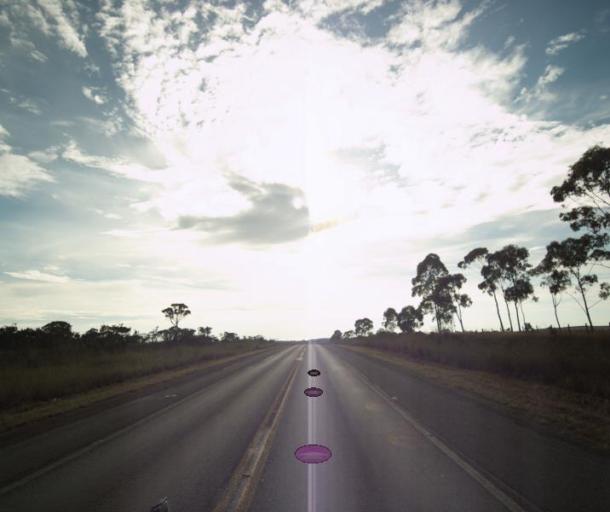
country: BR
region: Goias
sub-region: Pirenopolis
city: Pirenopolis
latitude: -15.7660
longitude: -48.7095
